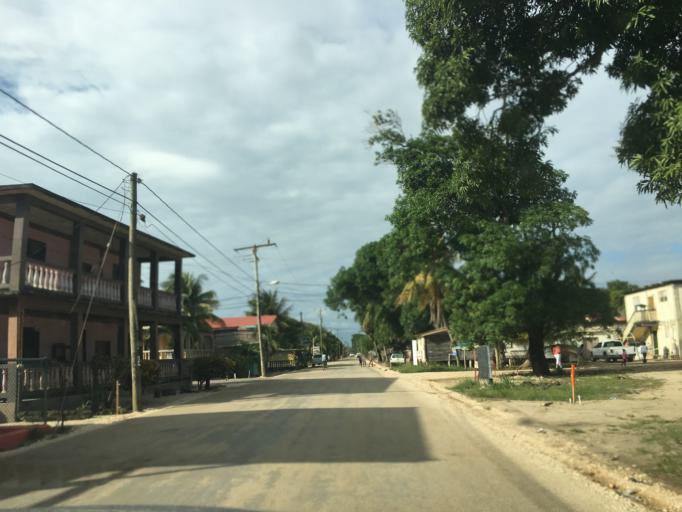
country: BZ
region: Stann Creek
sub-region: Dangriga
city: Dangriga
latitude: 16.8675
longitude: -88.2860
